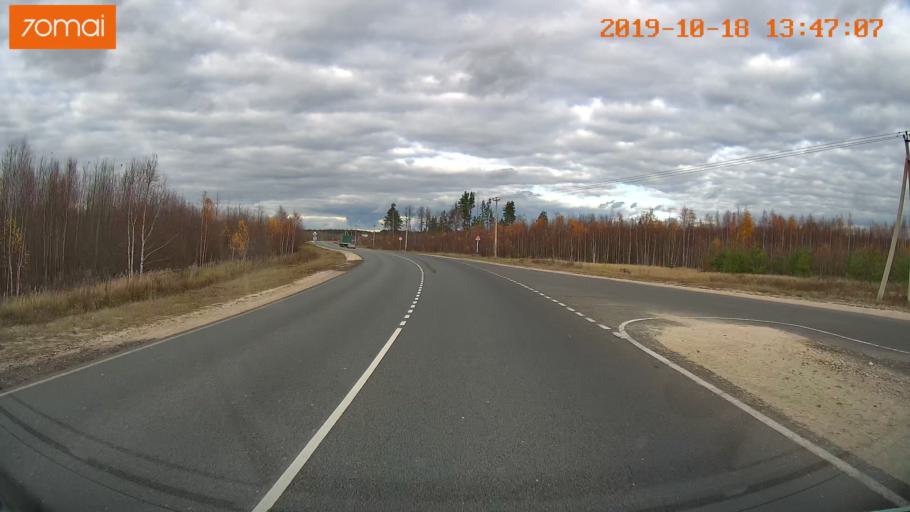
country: RU
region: Rjazan
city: Solotcha
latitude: 54.9700
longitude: 39.9515
